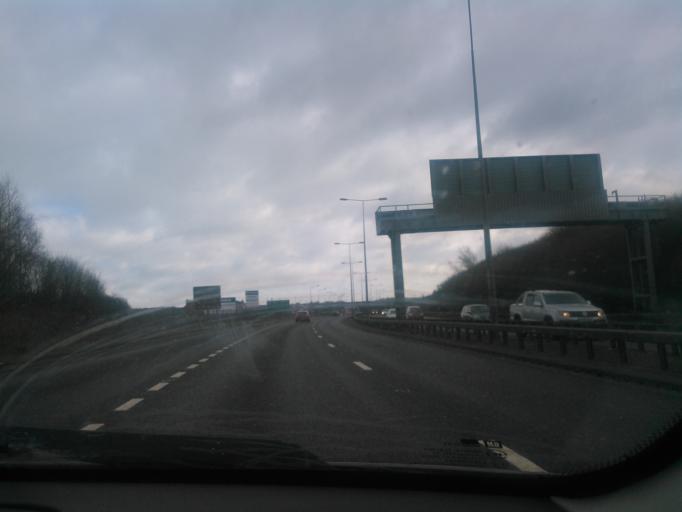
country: GB
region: England
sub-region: Staffordshire
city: Longton
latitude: 52.9914
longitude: -2.1503
